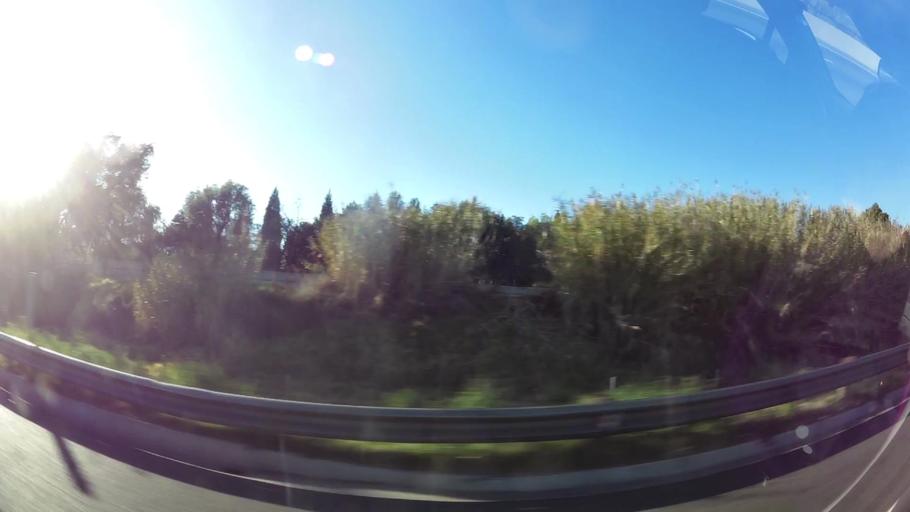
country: ZA
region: Gauteng
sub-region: City of Johannesburg Metropolitan Municipality
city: Roodepoort
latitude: -26.1424
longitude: 27.9321
